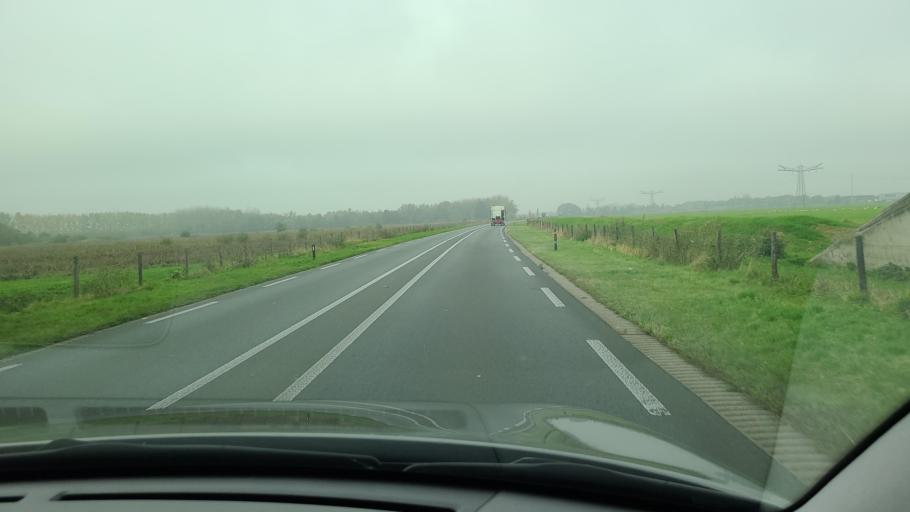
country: NL
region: Gelderland
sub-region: Gemeente Druten
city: Druten
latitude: 51.8708
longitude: 5.5496
